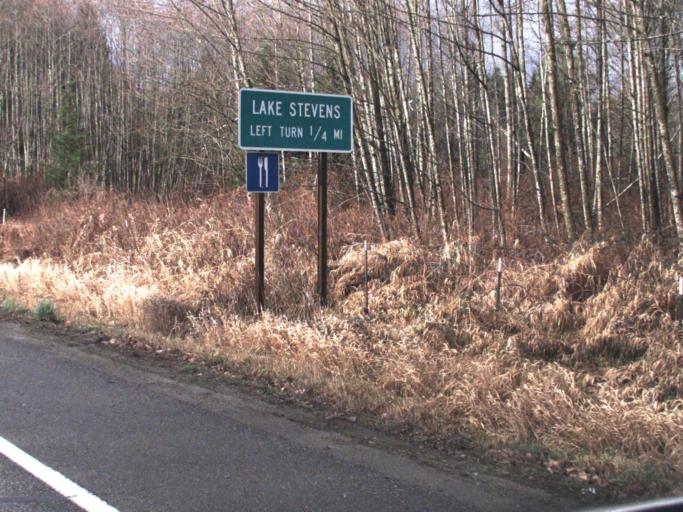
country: US
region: Washington
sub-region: Snohomish County
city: Lake Stevens
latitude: 48.0312
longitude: -122.0666
